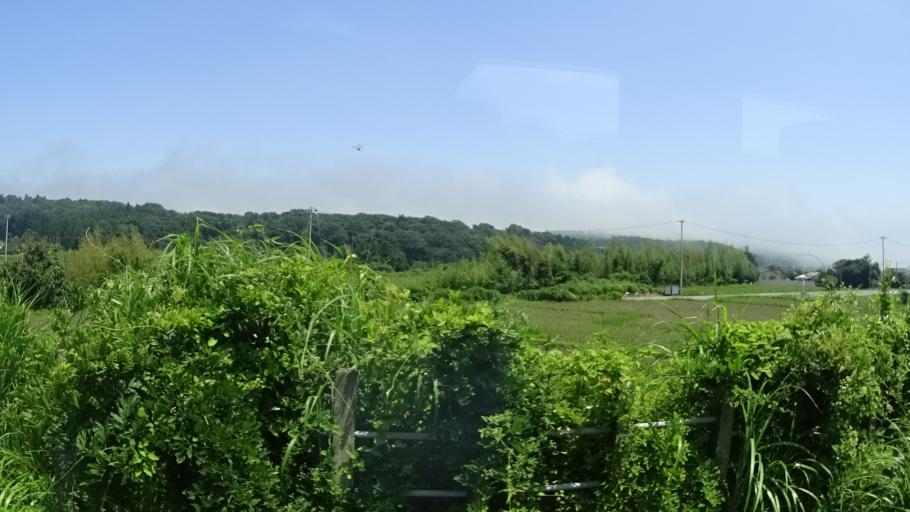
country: JP
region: Fukushima
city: Namie
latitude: 37.2843
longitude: 141.0025
